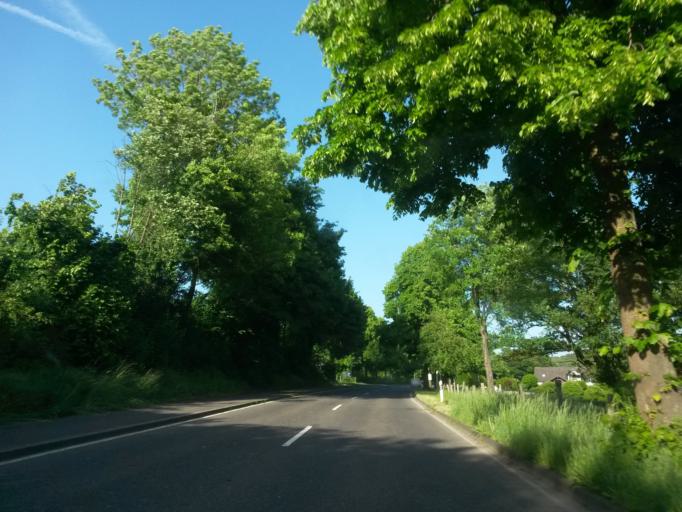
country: DE
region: North Rhine-Westphalia
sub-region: Regierungsbezirk Koln
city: Much
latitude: 50.8920
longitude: 7.3694
